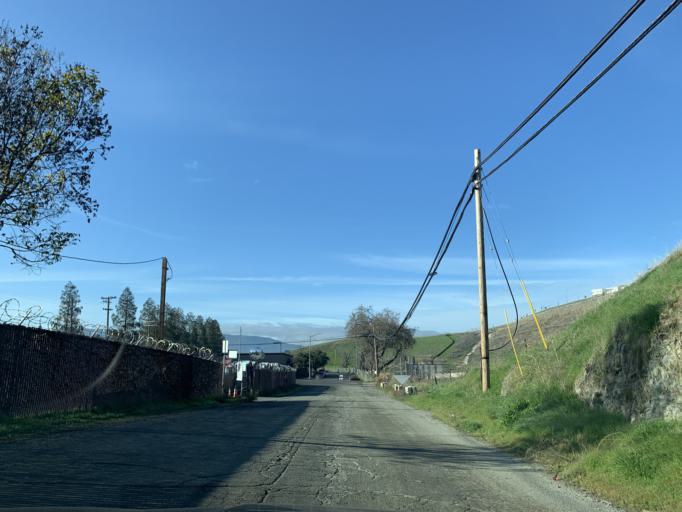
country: US
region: California
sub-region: Santa Clara County
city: Seven Trees
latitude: 37.2833
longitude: -121.8453
